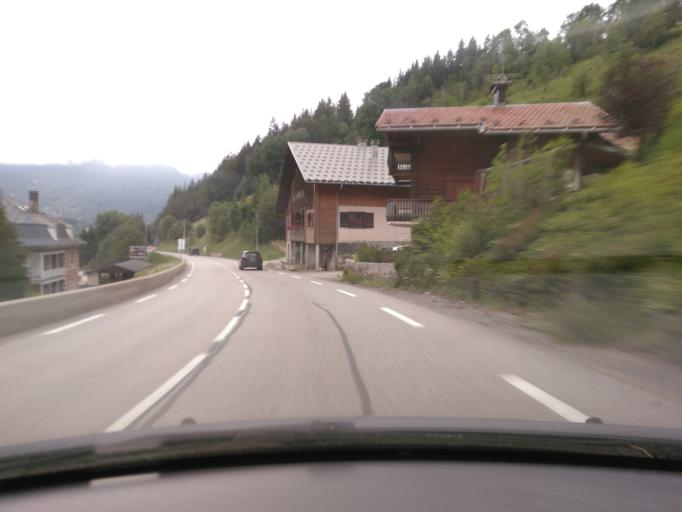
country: FR
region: Rhone-Alpes
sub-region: Departement de la Haute-Savoie
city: Saint-Jean-de-Sixt
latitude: 45.9168
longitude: 6.4197
